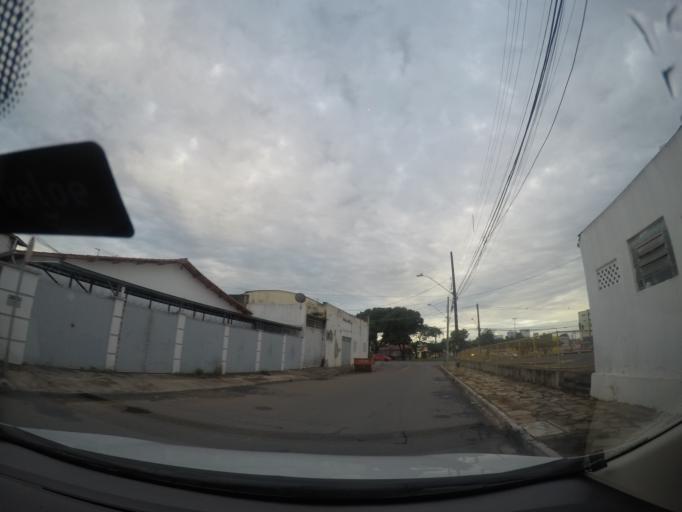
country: BR
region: Goias
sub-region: Goiania
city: Goiania
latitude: -16.6798
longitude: -49.2856
